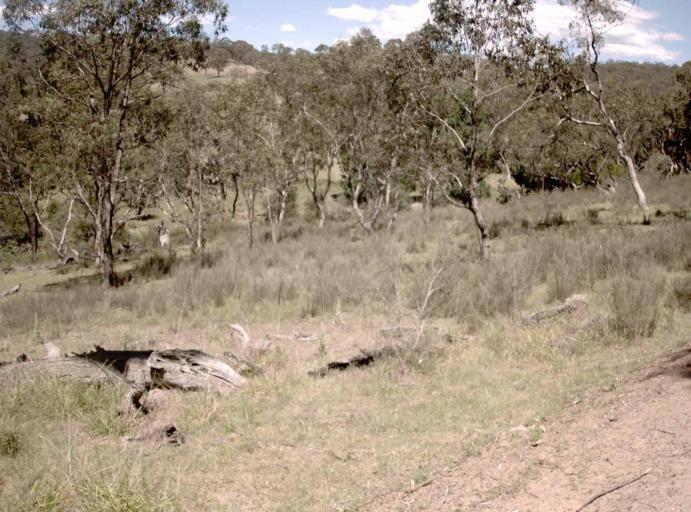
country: AU
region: New South Wales
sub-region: Snowy River
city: Jindabyne
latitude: -37.0414
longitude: 148.5590
